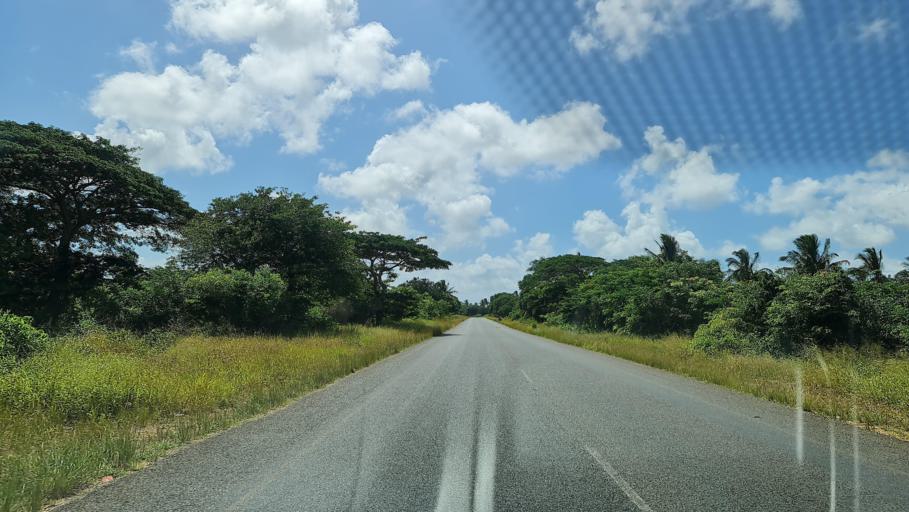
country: MZ
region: Inhambane
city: Maxixe
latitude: -24.5403
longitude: 34.9279
